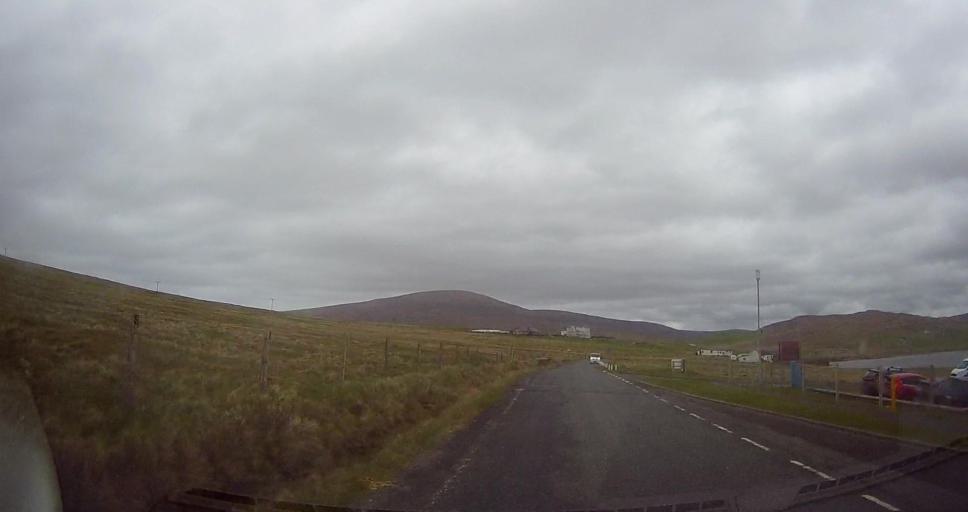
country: GB
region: Scotland
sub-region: Shetland Islands
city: Lerwick
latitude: 60.4878
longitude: -1.4671
